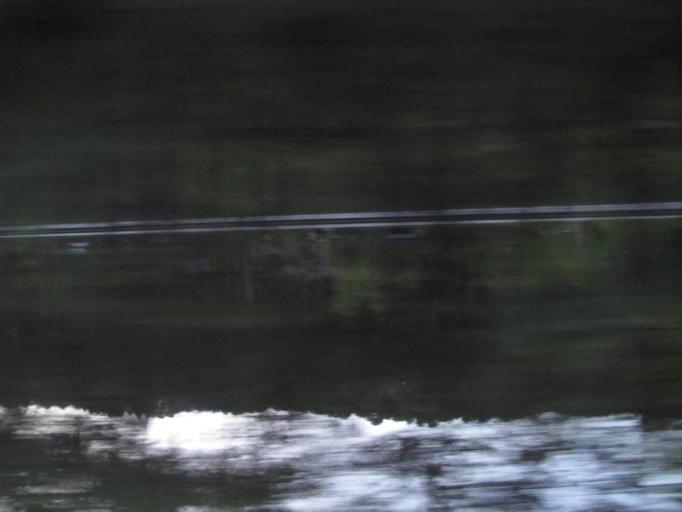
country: NO
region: Oppland
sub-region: Ringebu
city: Ringebu
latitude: 61.5508
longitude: 10.0524
